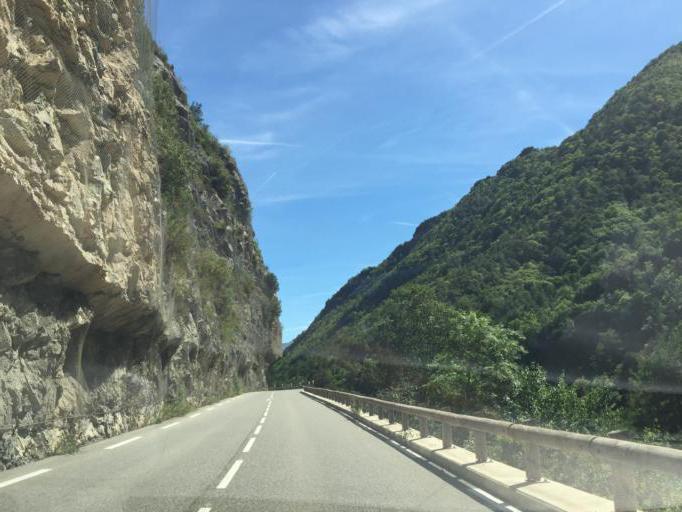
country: FR
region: Provence-Alpes-Cote d'Azur
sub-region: Departement des Alpes-Maritimes
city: Saint-Martin-Vesubie
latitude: 44.0380
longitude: 7.1275
